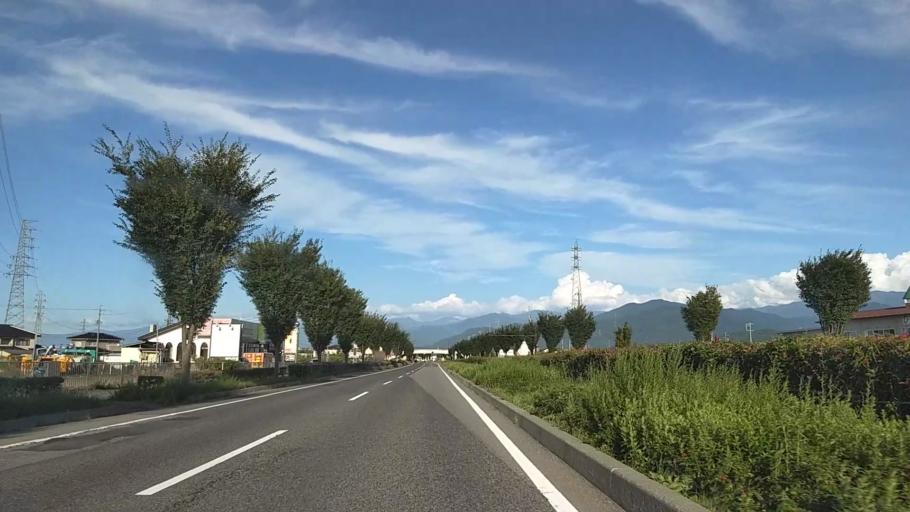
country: JP
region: Nagano
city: Nagano-shi
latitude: 36.6040
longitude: 138.1822
